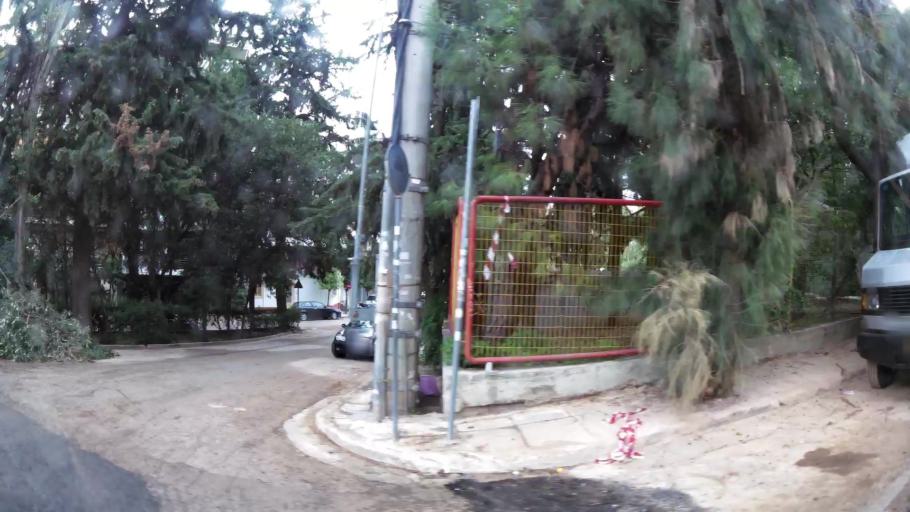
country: GR
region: Attica
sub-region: Nomarchia Athinas
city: Kaisariani
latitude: 37.9646
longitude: 23.7685
